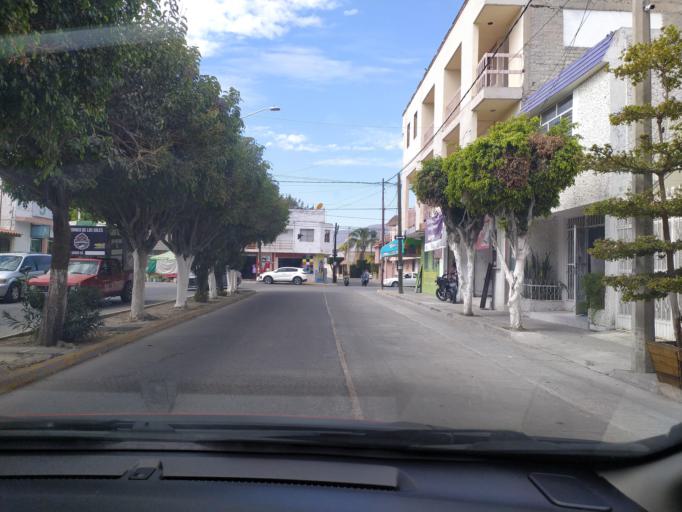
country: LA
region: Oudomxai
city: Muang La
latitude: 21.0124
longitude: 101.8585
